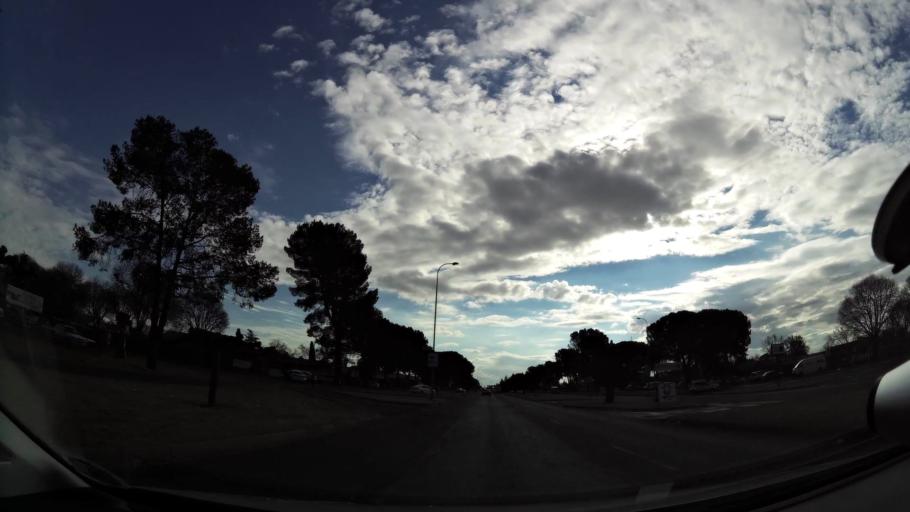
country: ZA
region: Orange Free State
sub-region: Lejweleputswa District Municipality
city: Welkom
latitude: -27.9858
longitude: 26.7521
